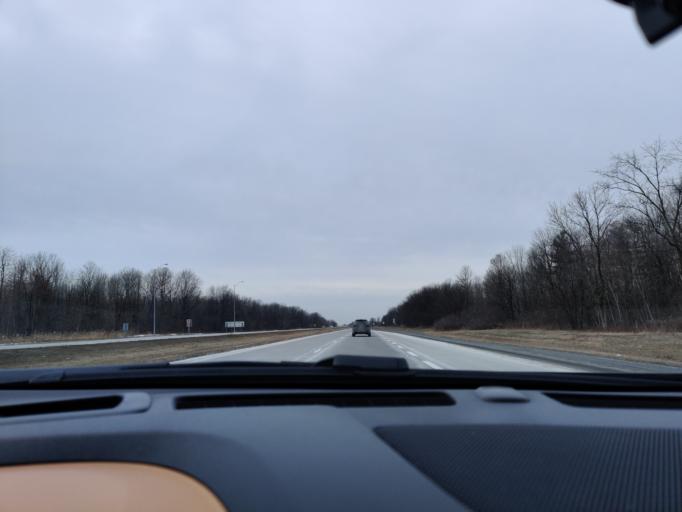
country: US
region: New York
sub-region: St. Lawrence County
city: Massena
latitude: 45.0466
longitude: -74.9081
